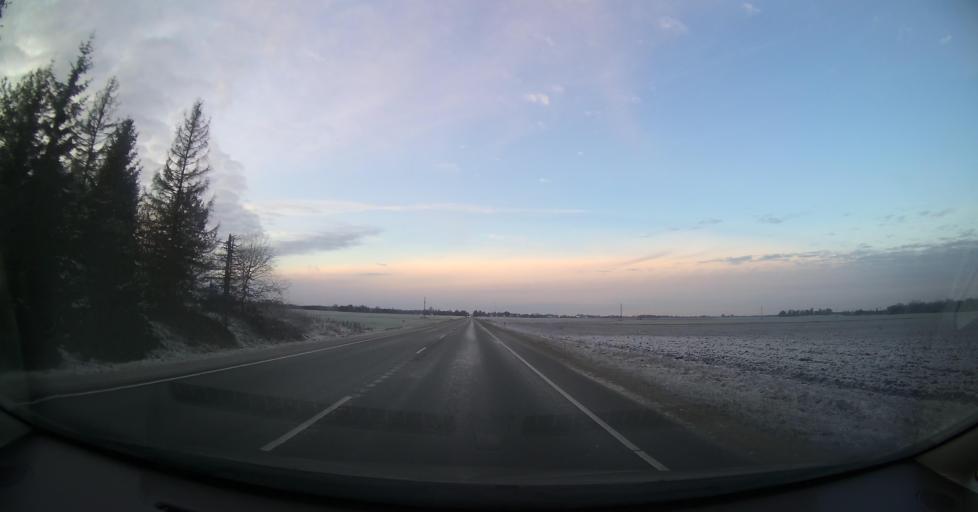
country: EE
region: Jogevamaa
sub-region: Poltsamaa linn
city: Poltsamaa
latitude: 58.6598
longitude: 26.0213
